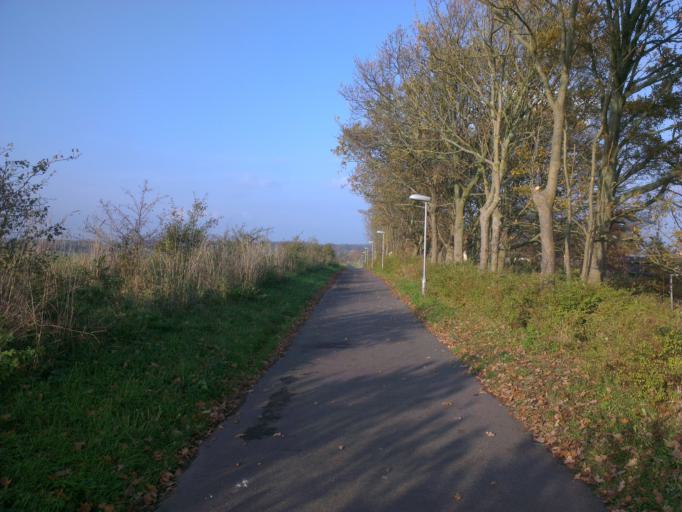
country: DK
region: Capital Region
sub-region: Frederikssund Kommune
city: Jaegerspris
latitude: 55.8450
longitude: 11.9855
